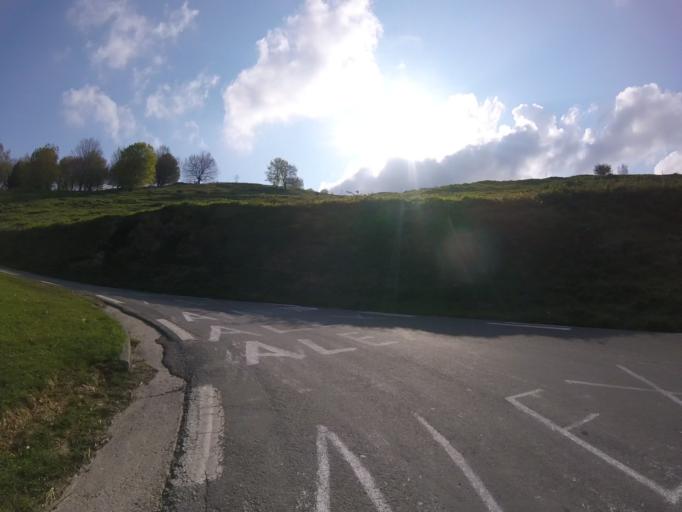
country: ES
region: Basque Country
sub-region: Provincia de Guipuzcoa
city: Azkoitia
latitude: 43.2213
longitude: -2.3111
